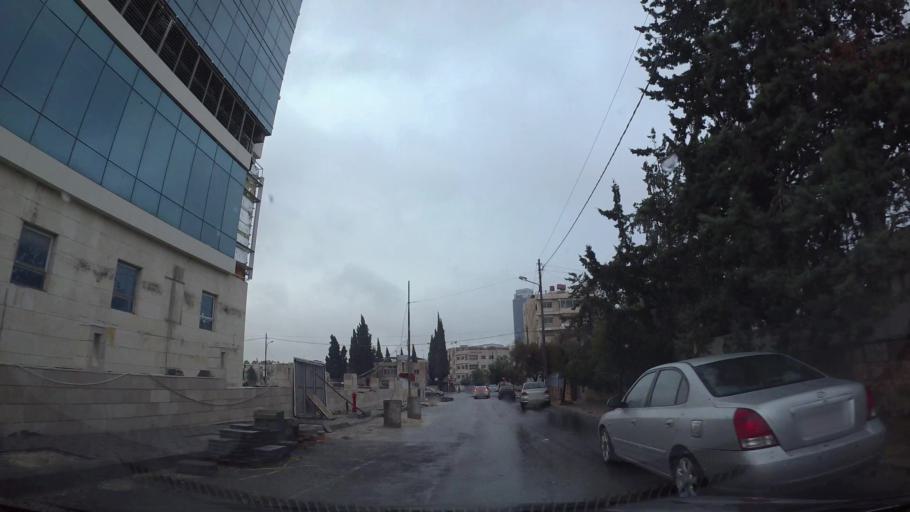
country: JO
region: Amman
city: Amman
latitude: 31.9692
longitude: 35.9114
